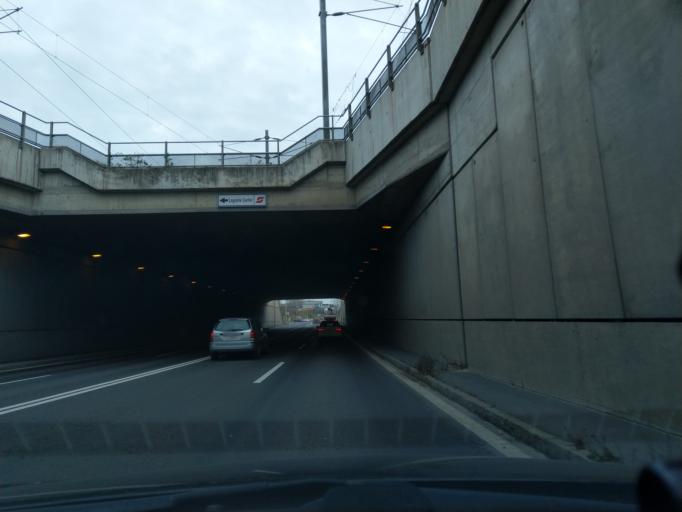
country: AT
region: Upper Austria
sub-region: Linz Stadt
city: Linz
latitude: 48.2724
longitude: 14.3200
